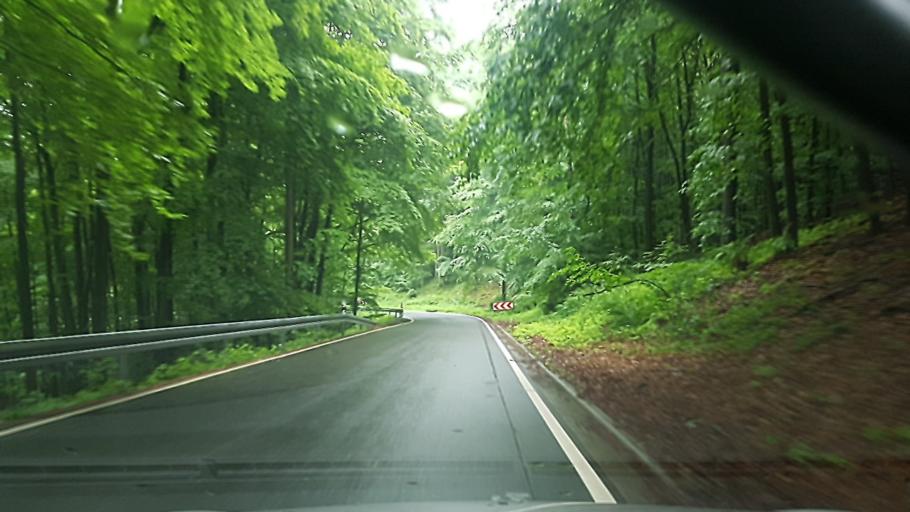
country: DE
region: Hesse
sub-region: Regierungsbezirk Darmstadt
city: Seeheim-Jugenheim
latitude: 49.7917
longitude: 8.6647
